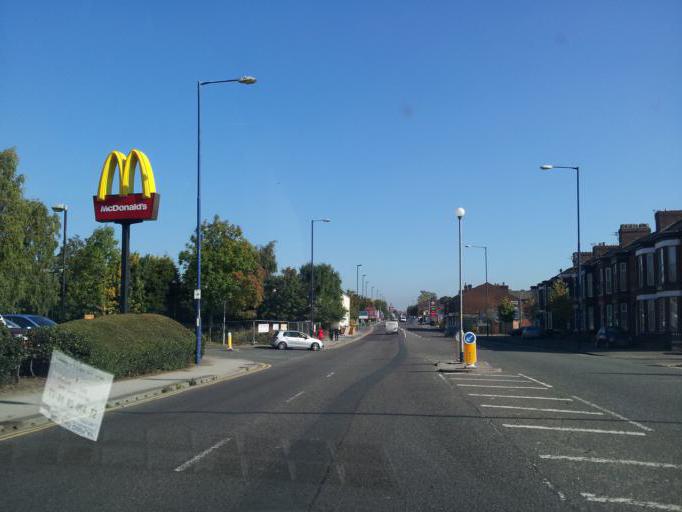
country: GB
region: England
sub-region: Manchester
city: Failsworth
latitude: 53.5036
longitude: -2.1780
